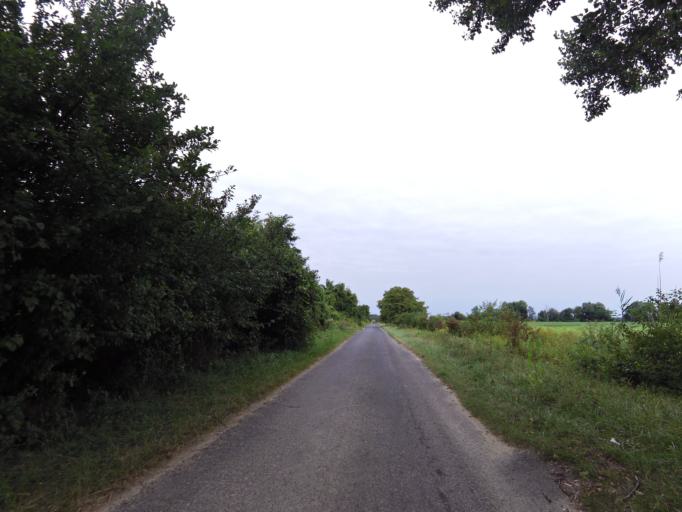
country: HU
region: Veszprem
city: Tapolca
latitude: 46.8423
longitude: 17.3655
